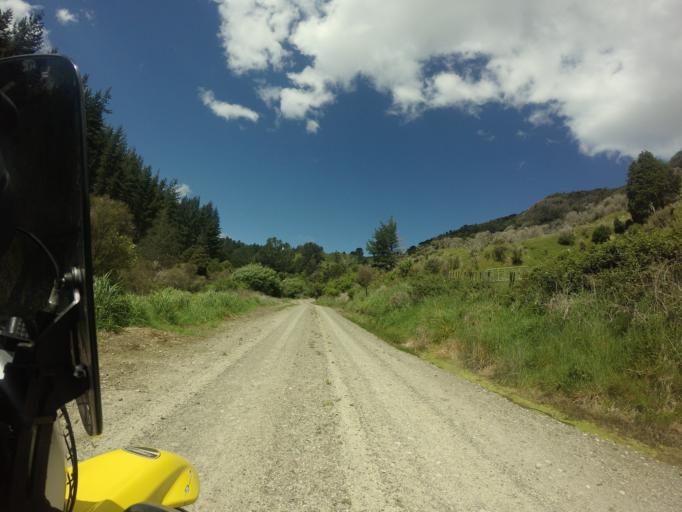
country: NZ
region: Hawke's Bay
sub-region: Wairoa District
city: Wairoa
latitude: -38.9732
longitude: 177.6768
